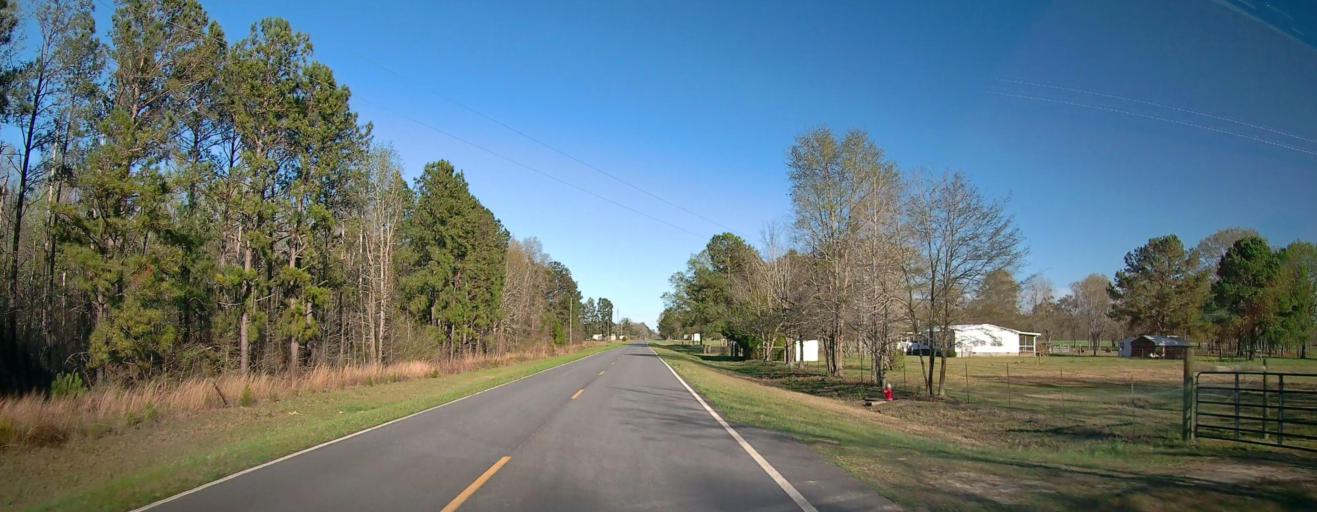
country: US
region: Georgia
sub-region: Pulaski County
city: Hawkinsville
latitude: 32.3478
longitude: -83.5967
